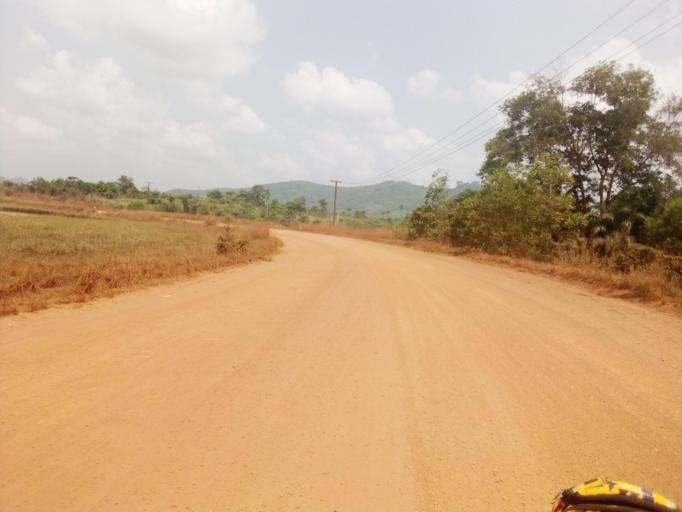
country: SL
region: Southern Province
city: Mogbwemo
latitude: 7.6678
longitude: -12.2783
